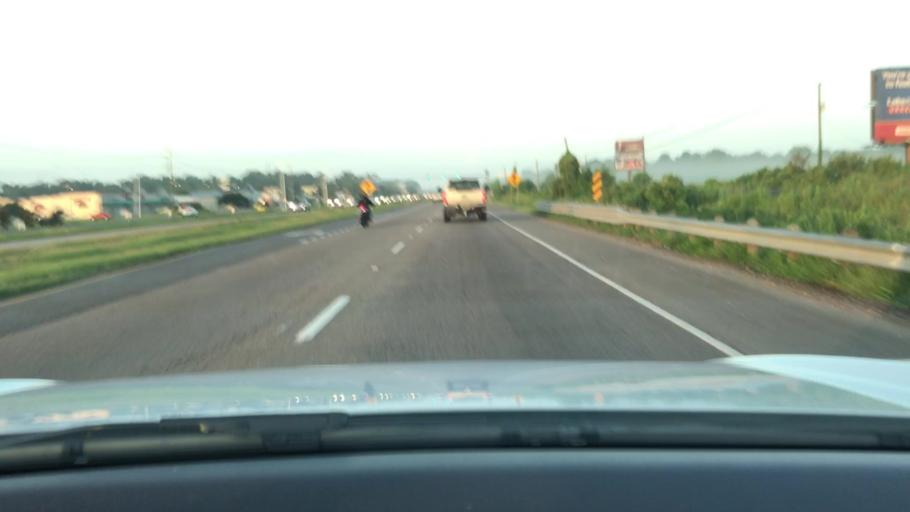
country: US
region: Louisiana
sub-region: West Baton Rouge Parish
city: Port Allen
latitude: 30.4230
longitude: -91.2183
